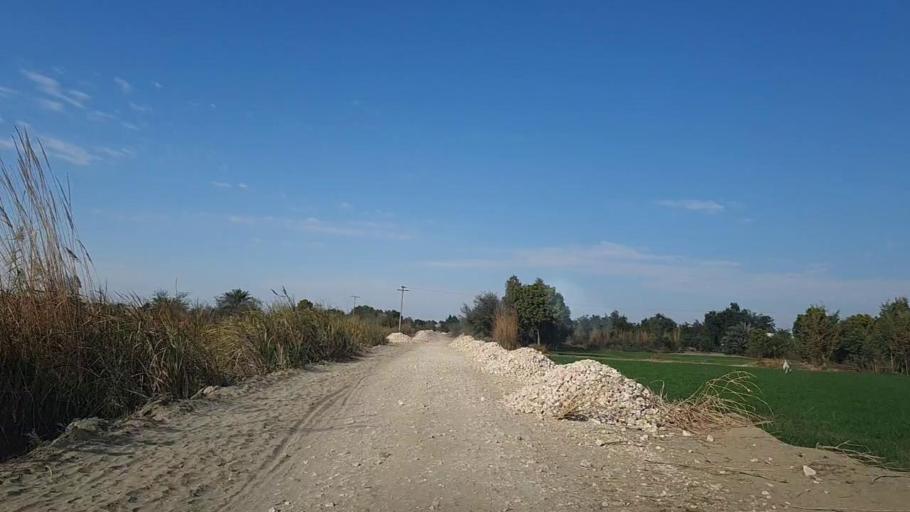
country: PK
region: Sindh
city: Jam Sahib
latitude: 26.3054
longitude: 68.8141
